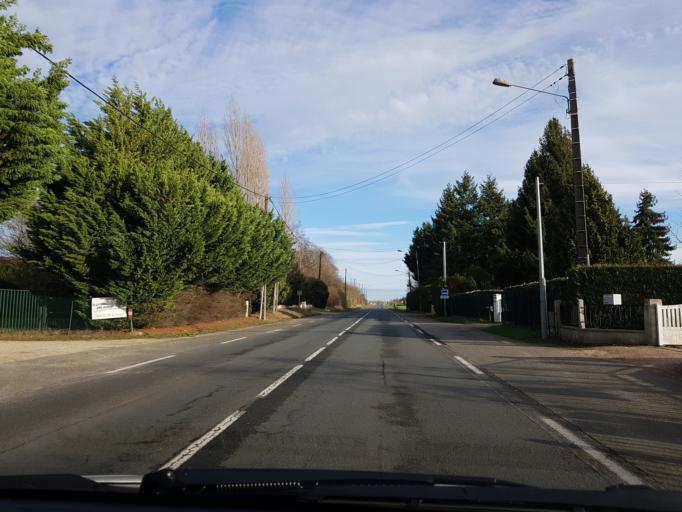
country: FR
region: Centre
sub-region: Departement du Loiret
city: Sandillon
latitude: 47.8505
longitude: 2.0569
